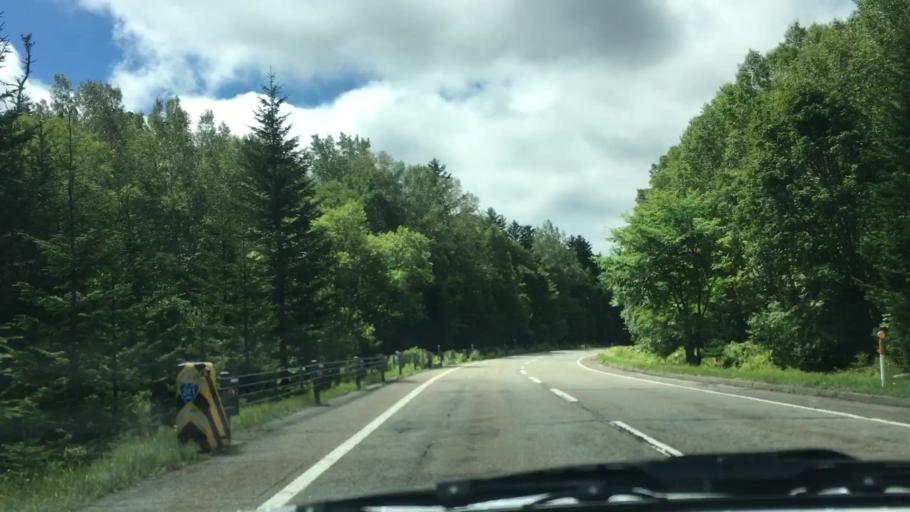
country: JP
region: Hokkaido
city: Kitami
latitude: 43.4150
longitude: 143.9734
